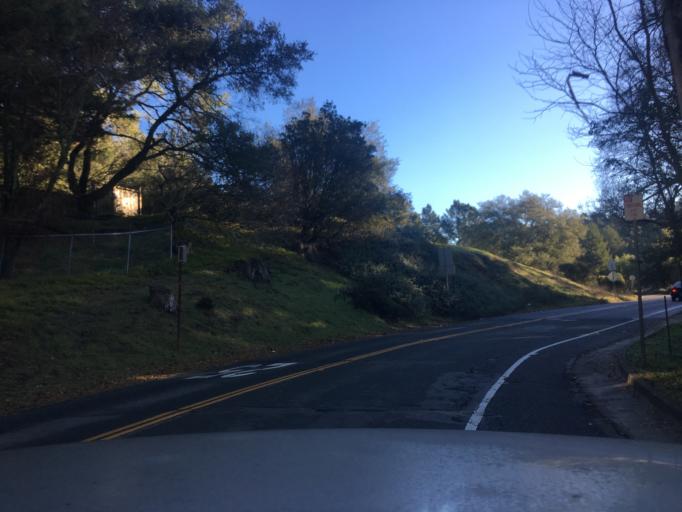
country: US
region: California
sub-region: Alameda County
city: Berkeley
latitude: 37.8832
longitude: -122.2471
